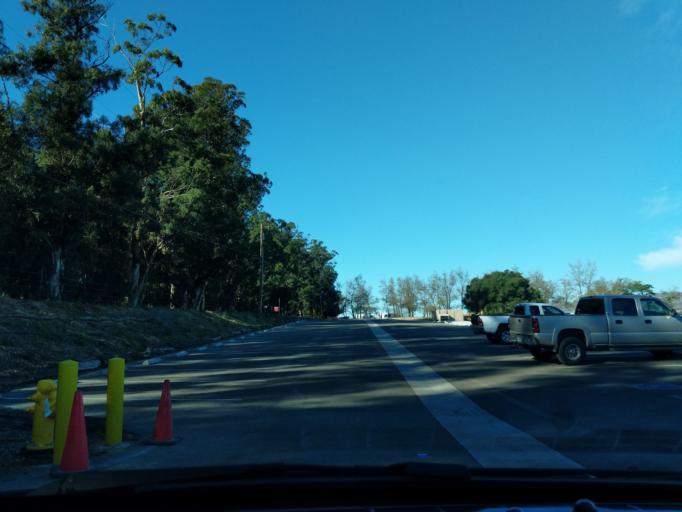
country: US
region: California
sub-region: San Luis Obispo County
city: Nipomo
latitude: 35.0258
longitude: -120.4693
